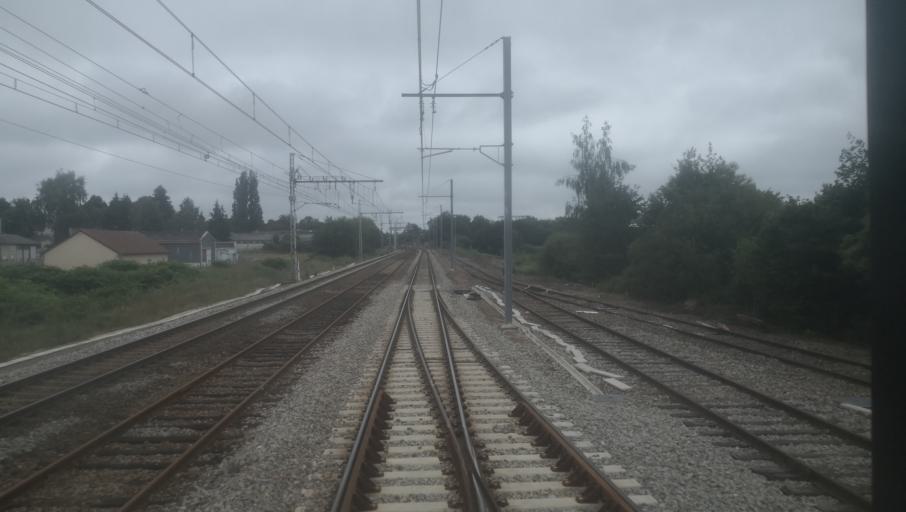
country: FR
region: Limousin
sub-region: Departement de la Creuse
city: La Souterraine
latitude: 46.2435
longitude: 1.4893
